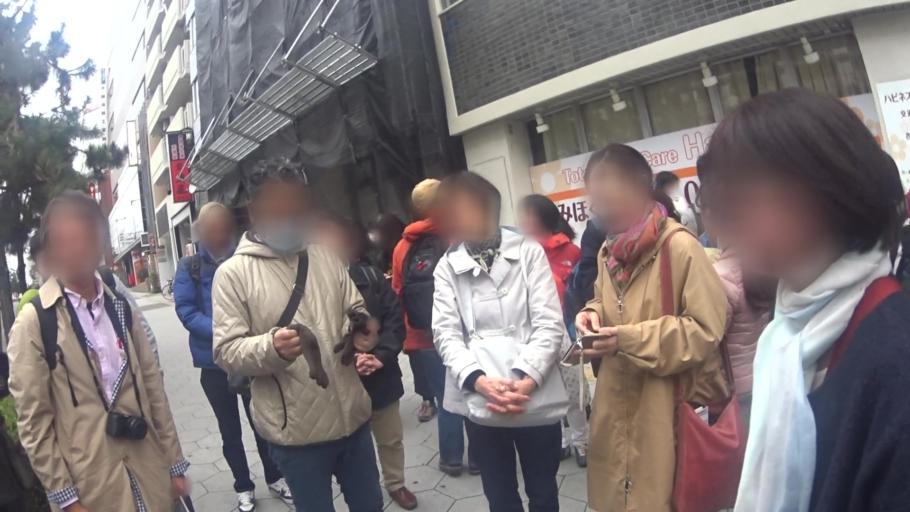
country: JP
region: Osaka
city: Osaka-shi
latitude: 34.6635
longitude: 135.5288
